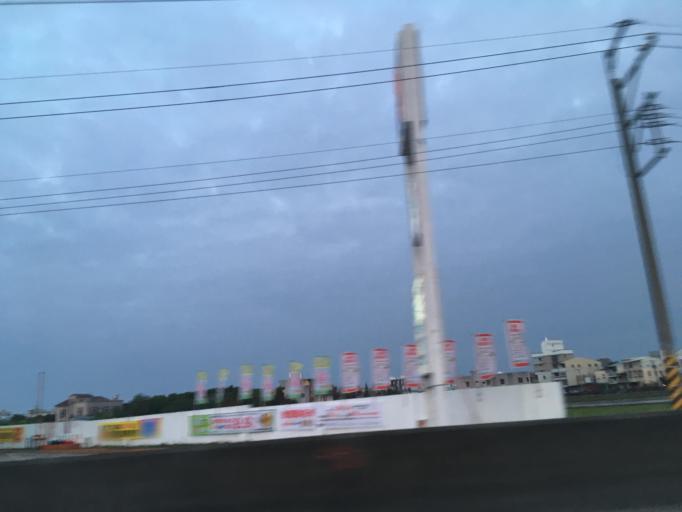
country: TW
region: Taiwan
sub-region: Chiayi
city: Jiayi Shi
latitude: 23.6031
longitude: 120.4482
